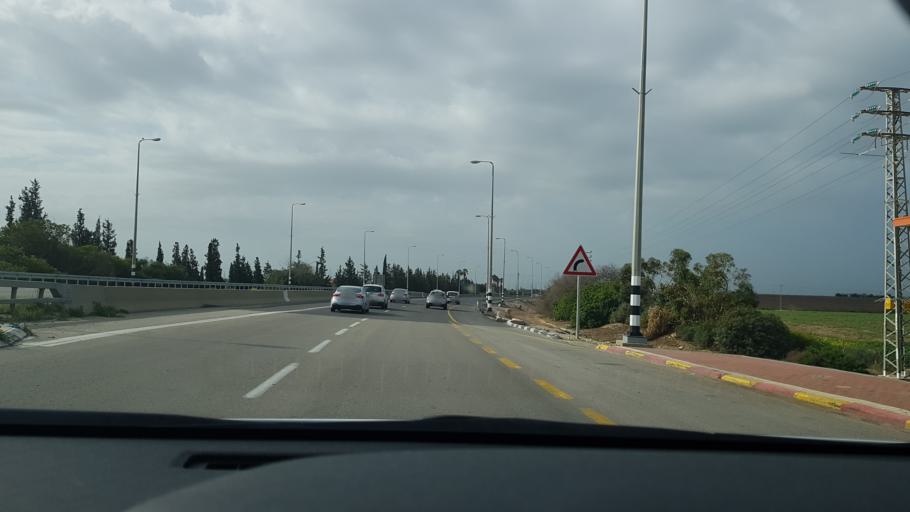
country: IL
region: Southern District
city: Ashqelon
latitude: 31.6532
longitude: 34.5984
